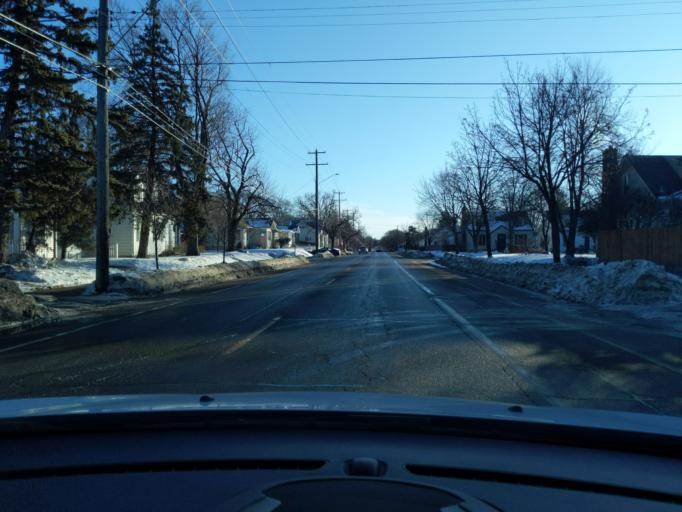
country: US
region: Minnesota
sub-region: Hennepin County
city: Minneapolis
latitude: 44.9269
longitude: -93.2393
